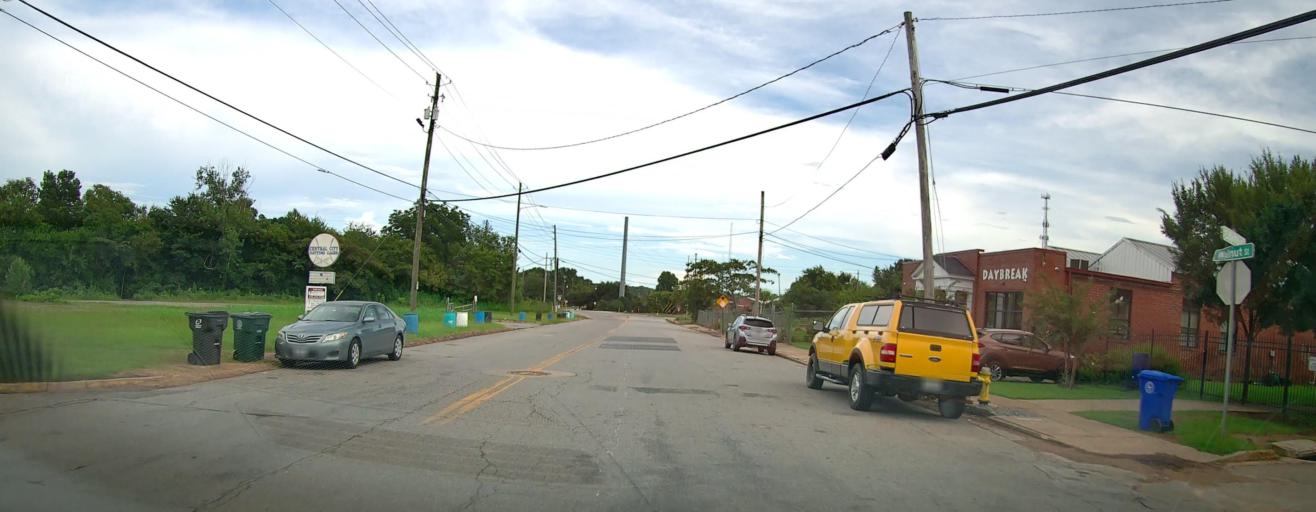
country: US
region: Georgia
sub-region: Bibb County
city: Macon
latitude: 32.8355
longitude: -83.6207
